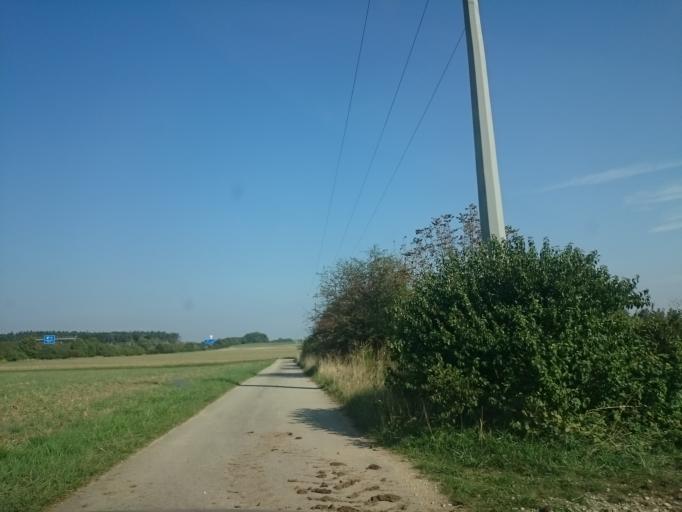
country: DE
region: Bavaria
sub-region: Regierungsbezirk Mittelfranken
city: Thalmassing
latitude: 49.1453
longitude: 11.2677
